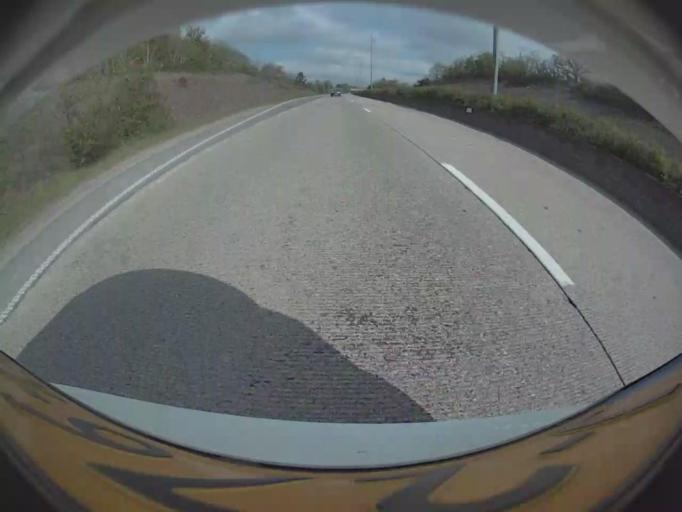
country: BE
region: Wallonia
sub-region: Province de Namur
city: Somme-Leuze
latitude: 50.3118
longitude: 5.3400
